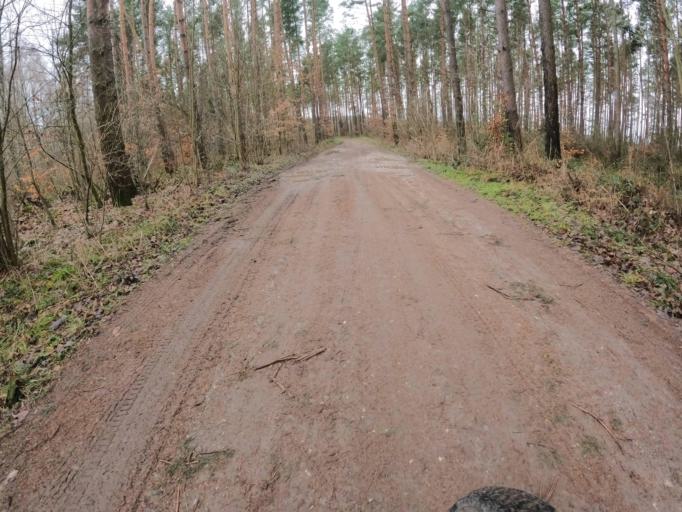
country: PL
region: West Pomeranian Voivodeship
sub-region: Powiat slawienski
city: Slawno
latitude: 54.2519
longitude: 16.6422
